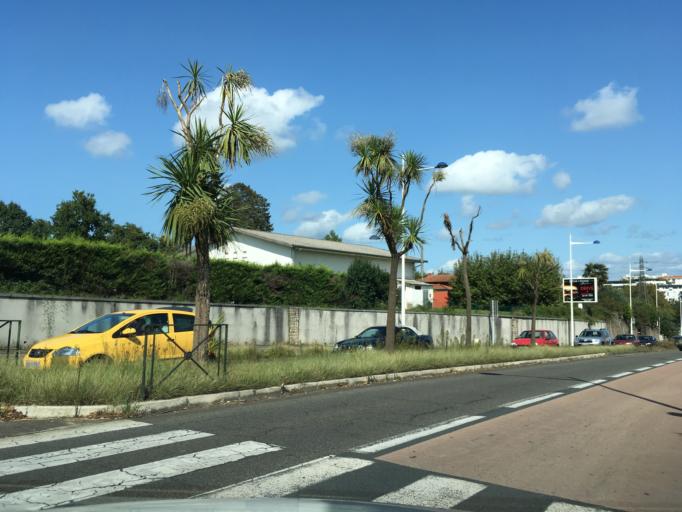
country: FR
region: Aquitaine
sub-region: Departement des Pyrenees-Atlantiques
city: Bayonne
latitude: 43.4852
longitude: -1.4940
